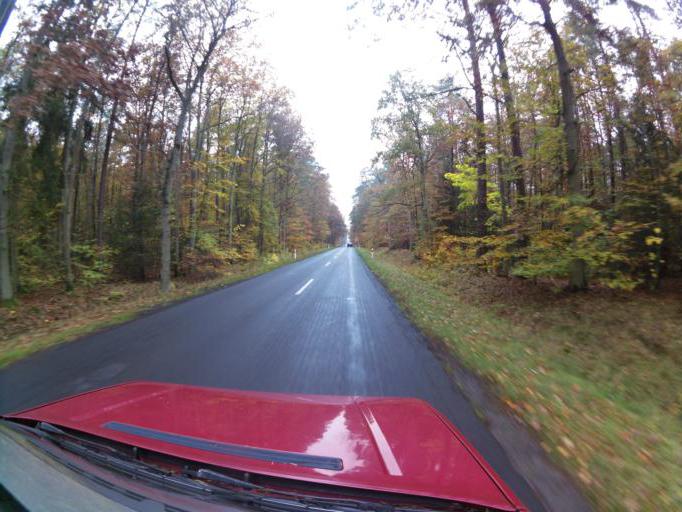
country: PL
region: West Pomeranian Voivodeship
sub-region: Powiat policki
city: Dobra
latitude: 53.5575
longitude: 14.4515
